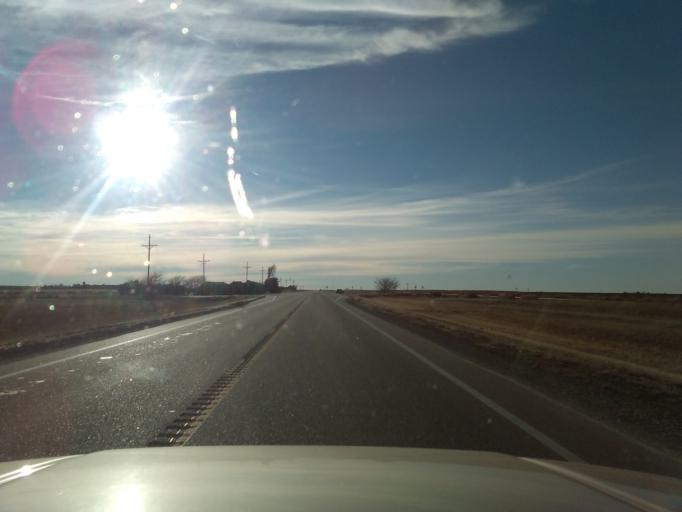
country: US
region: Kansas
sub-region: Sheridan County
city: Hoxie
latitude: 39.5395
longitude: -100.5787
